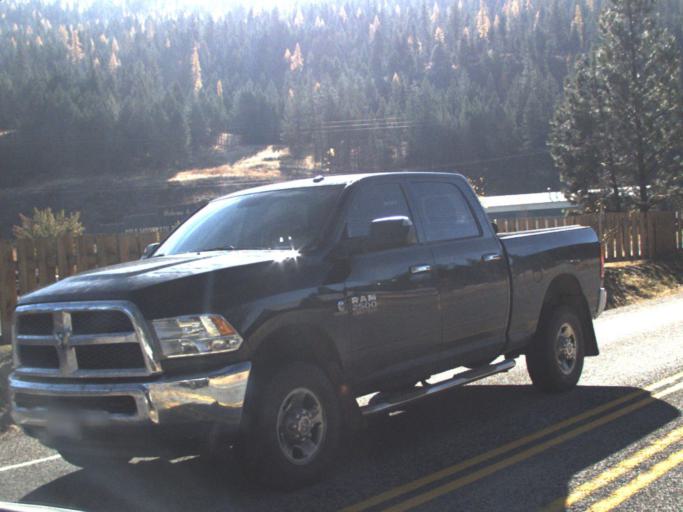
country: US
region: Washington
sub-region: Ferry County
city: Republic
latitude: 48.6527
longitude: -118.6715
